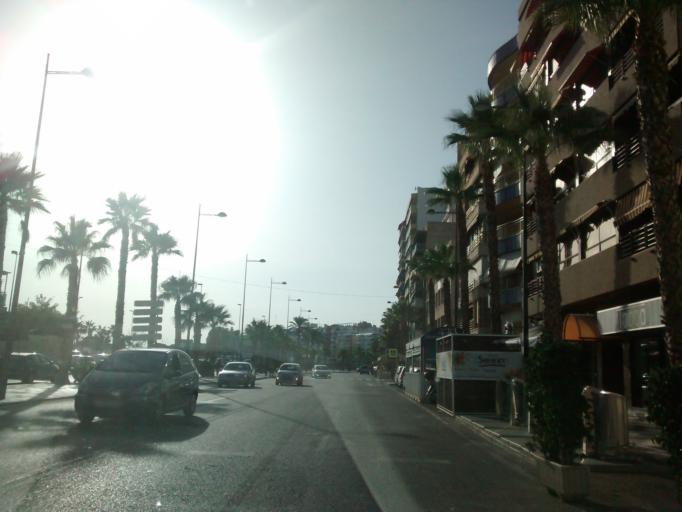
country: ES
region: Valencia
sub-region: Provincia de Alicante
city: Santa Pola
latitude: 38.1905
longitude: -0.5569
